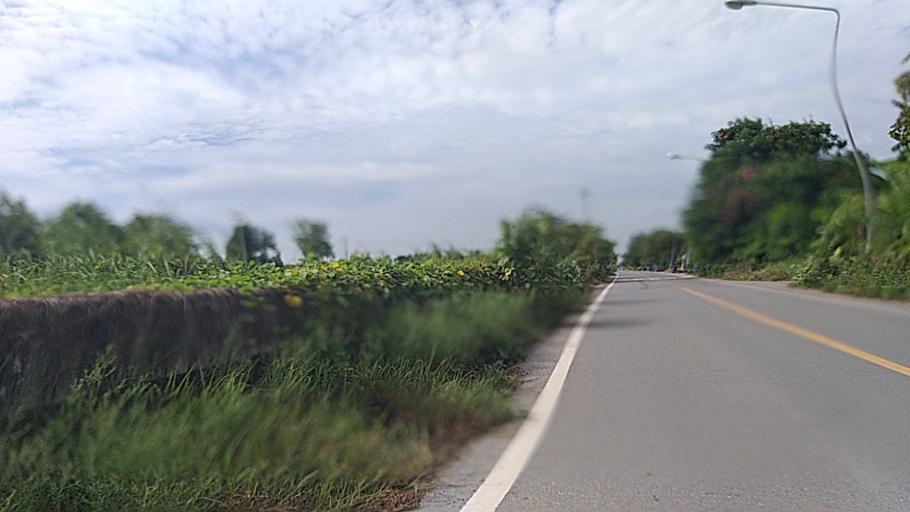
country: TH
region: Pathum Thani
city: Nong Suea
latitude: 14.0561
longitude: 100.8926
